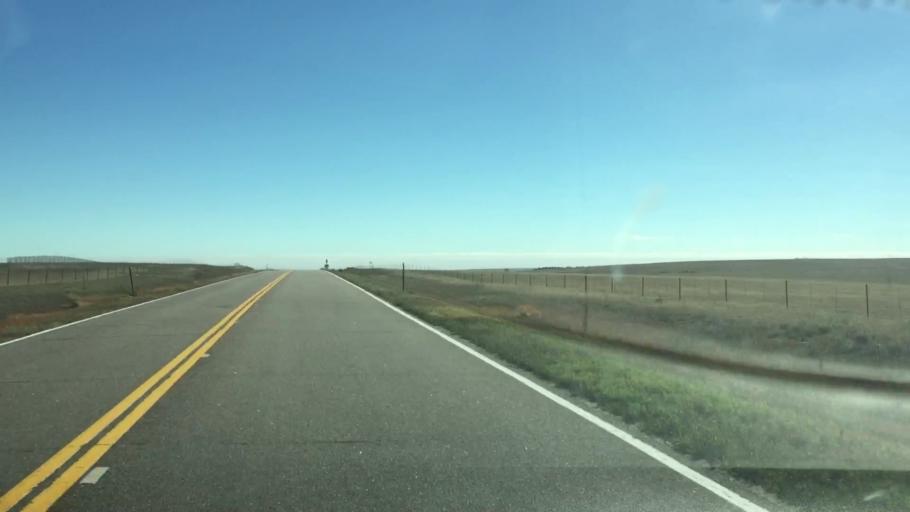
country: US
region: Colorado
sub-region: Lincoln County
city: Limon
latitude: 39.2880
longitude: -103.9717
